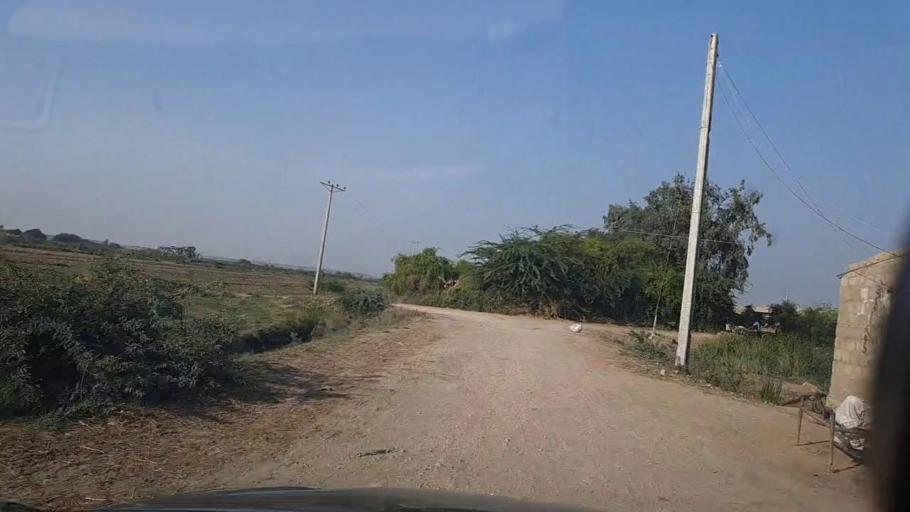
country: PK
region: Sindh
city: Thatta
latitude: 24.6029
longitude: 67.8745
